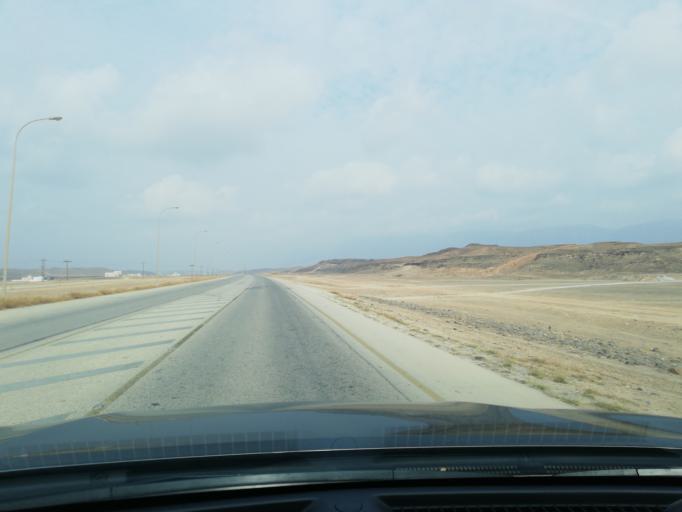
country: OM
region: Zufar
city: Salalah
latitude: 16.9560
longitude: 53.9109
